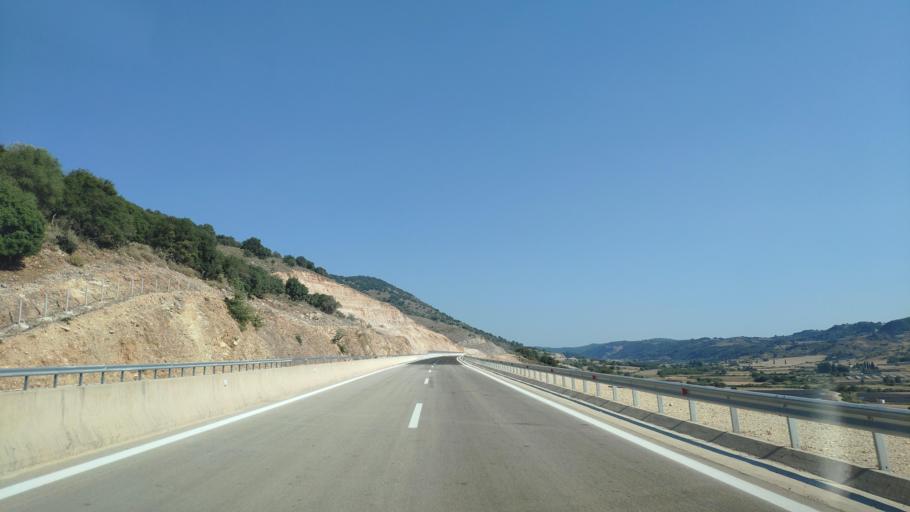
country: GR
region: West Greece
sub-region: Nomos Aitolias kai Akarnanias
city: Katouna
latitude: 38.8275
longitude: 21.1215
